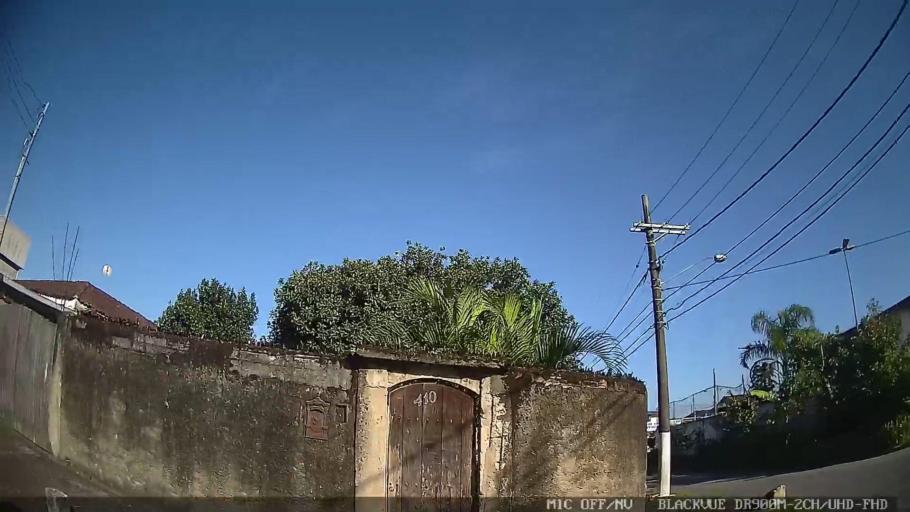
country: BR
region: Sao Paulo
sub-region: Guaruja
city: Guaruja
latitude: -23.9575
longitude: -46.2840
